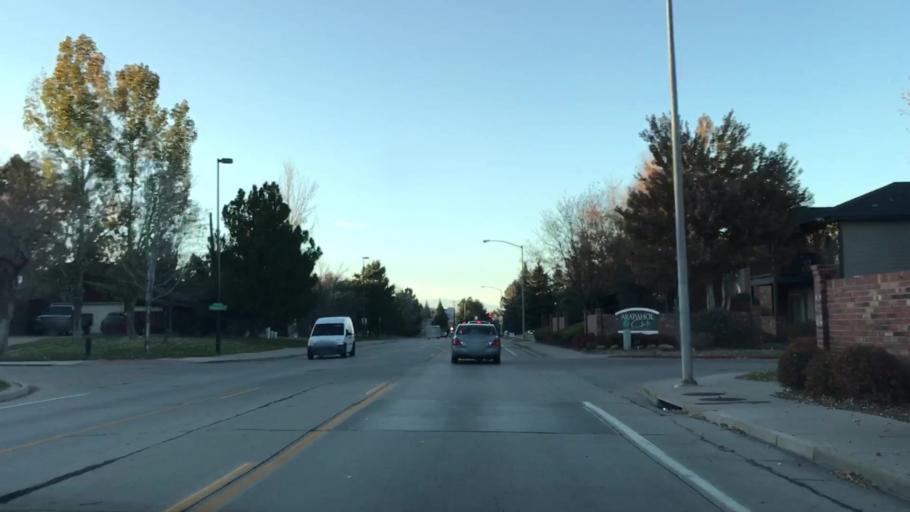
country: US
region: Colorado
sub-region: Arapahoe County
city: Glendale
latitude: 39.6659
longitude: -104.8920
